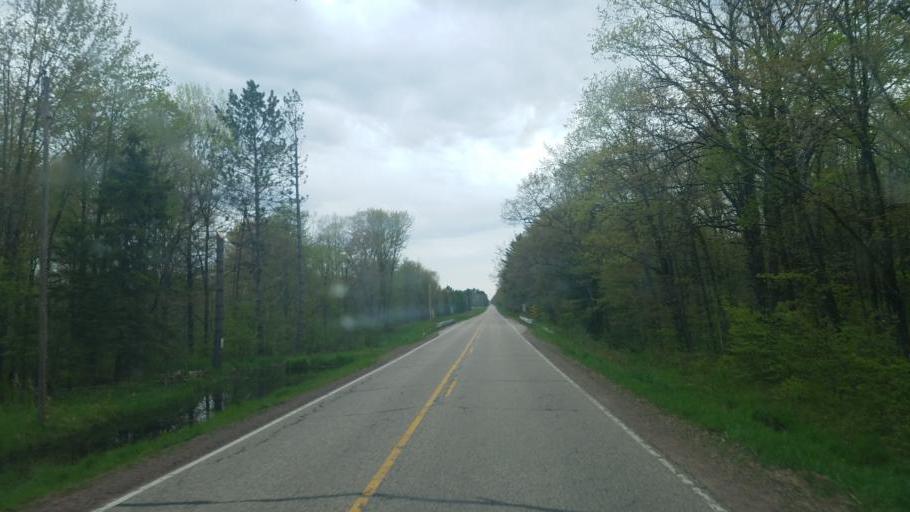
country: US
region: Wisconsin
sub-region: Wood County
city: Marshfield
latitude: 44.5149
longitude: -90.2994
